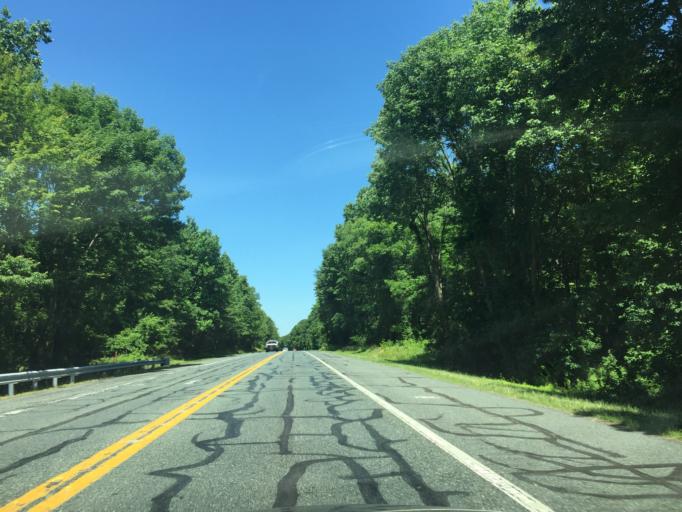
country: US
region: Maryland
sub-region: Harford County
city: Jarrettsville
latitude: 39.5806
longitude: -76.4488
